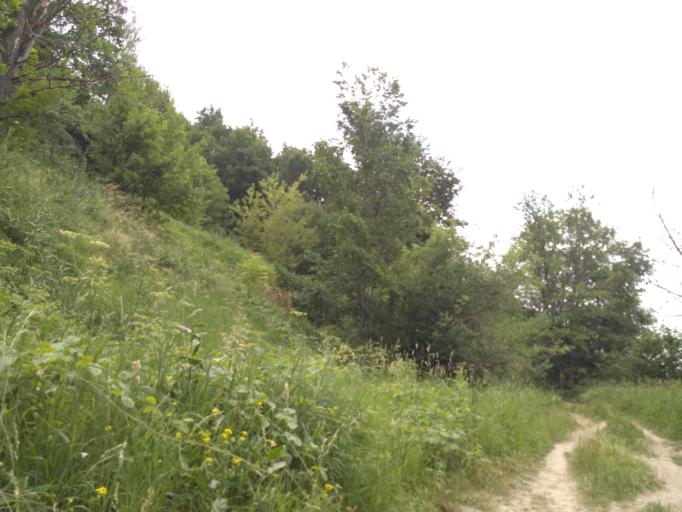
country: RU
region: Nizjnij Novgorod
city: Nizhniy Novgorod
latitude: 56.2704
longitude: 43.9725
